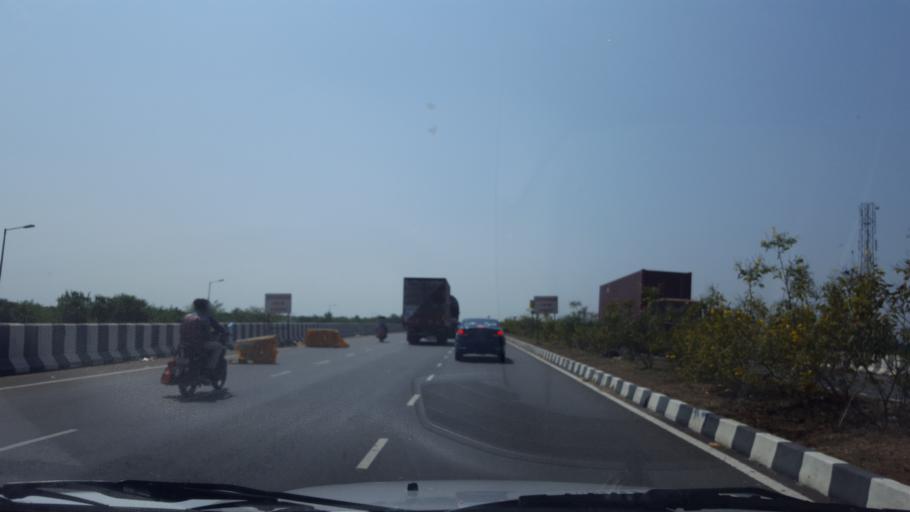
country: IN
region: Andhra Pradesh
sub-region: Prakasam
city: Addanki
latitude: 15.8059
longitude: 80.0411
